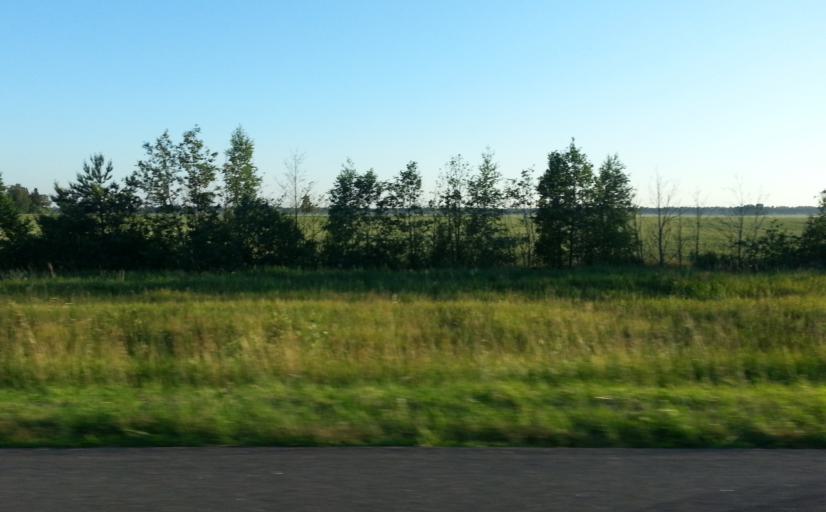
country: LT
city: Ramygala
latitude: 55.5362
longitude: 24.5433
